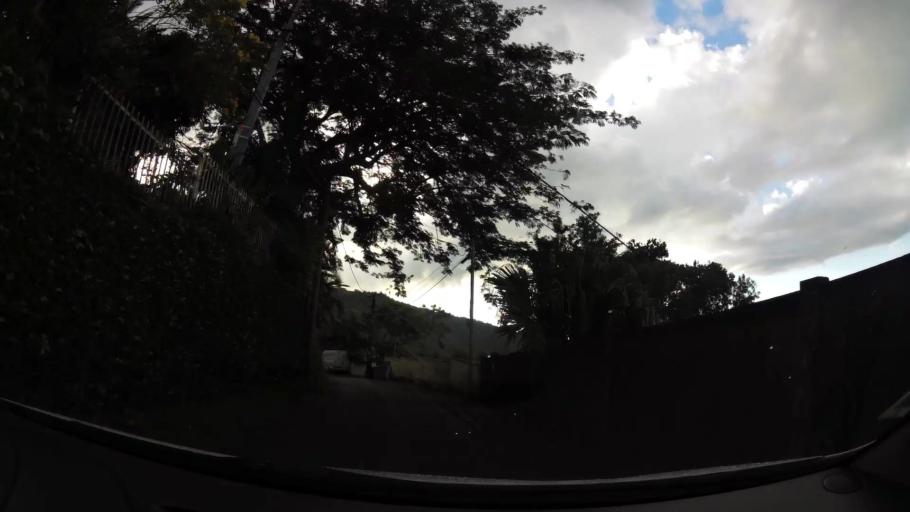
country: RE
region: Reunion
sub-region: Reunion
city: Saint-Denis
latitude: -20.9051
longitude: 55.4456
